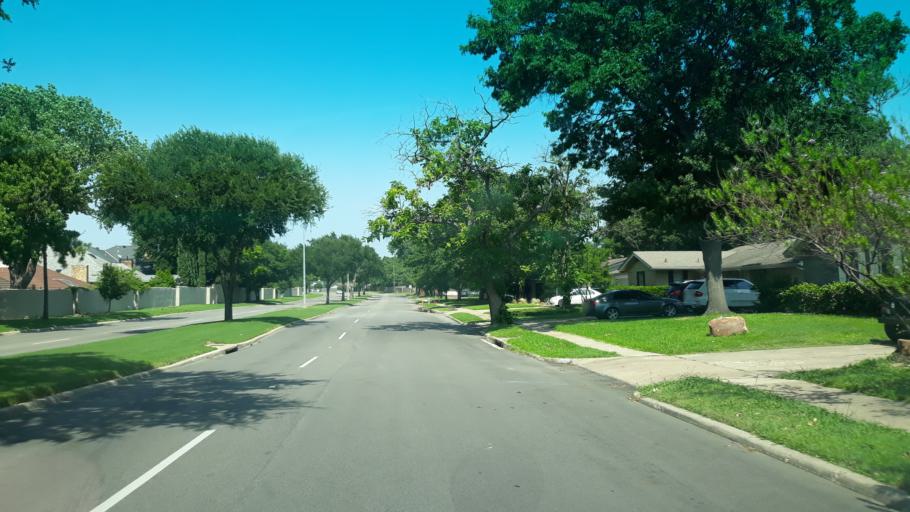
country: US
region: Texas
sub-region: Dallas County
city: Irving
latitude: 32.8559
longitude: -96.9668
